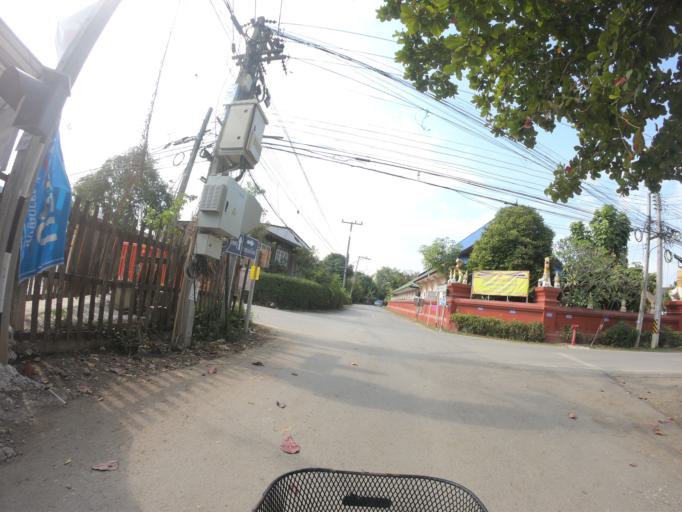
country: TH
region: Chiang Mai
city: Saraphi
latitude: 18.7318
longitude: 99.0600
